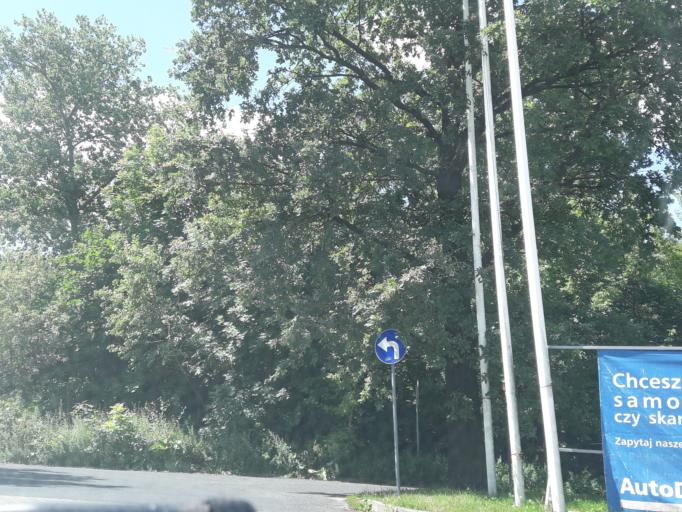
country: PL
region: Lublin Voivodeship
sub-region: Powiat lubelski
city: Lublin
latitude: 51.2504
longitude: 22.5233
